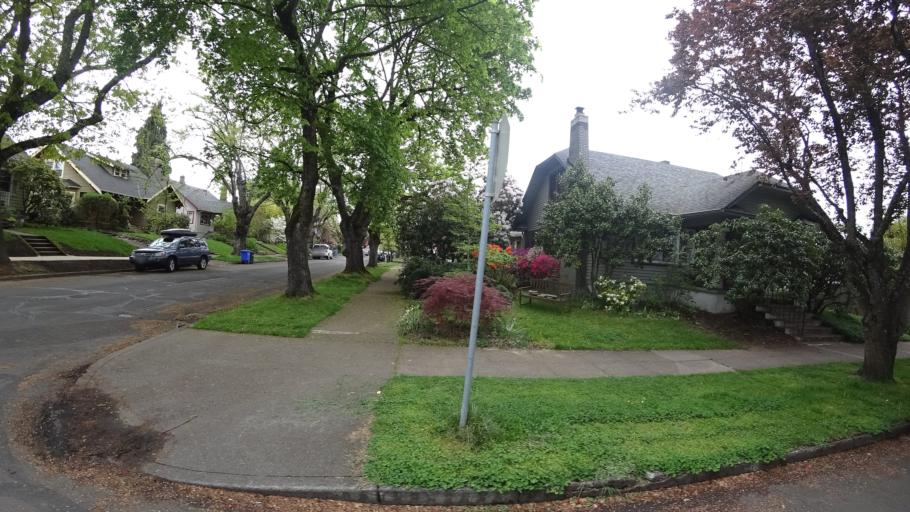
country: US
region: Oregon
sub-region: Clackamas County
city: Milwaukie
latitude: 45.4757
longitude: -122.6458
